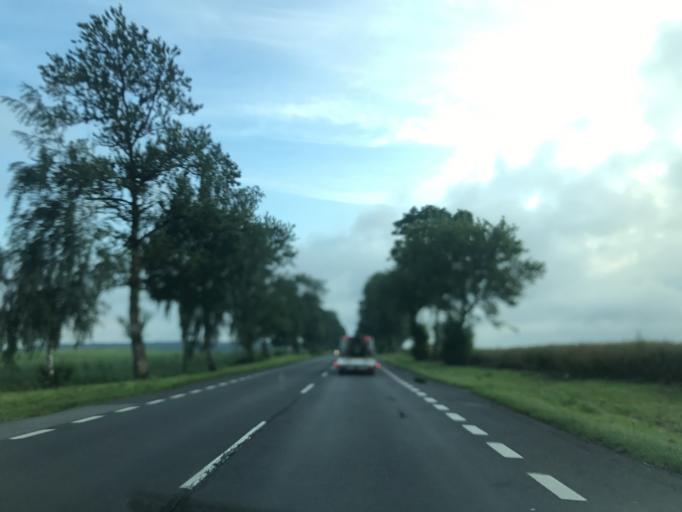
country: PL
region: West Pomeranian Voivodeship
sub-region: Powiat kolobrzeski
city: Goscino
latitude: 53.9784
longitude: 15.6886
